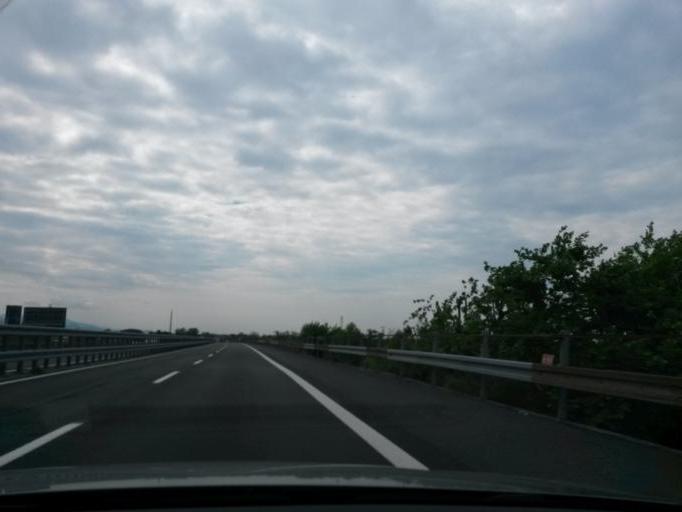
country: IT
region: Tuscany
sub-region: Provincia di Lucca
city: Pietrasanta
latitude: 43.9243
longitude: 10.2268
